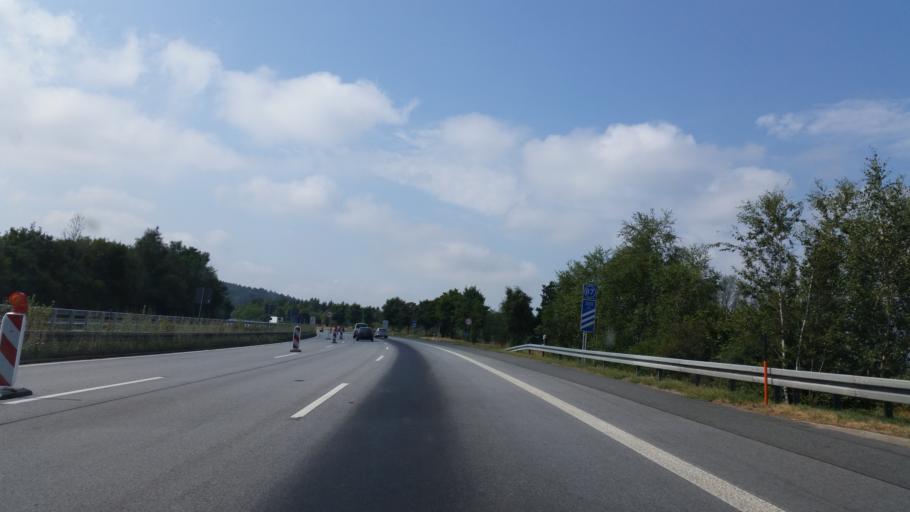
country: DE
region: Saxony
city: Burkau
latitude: 51.1810
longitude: 14.1497
